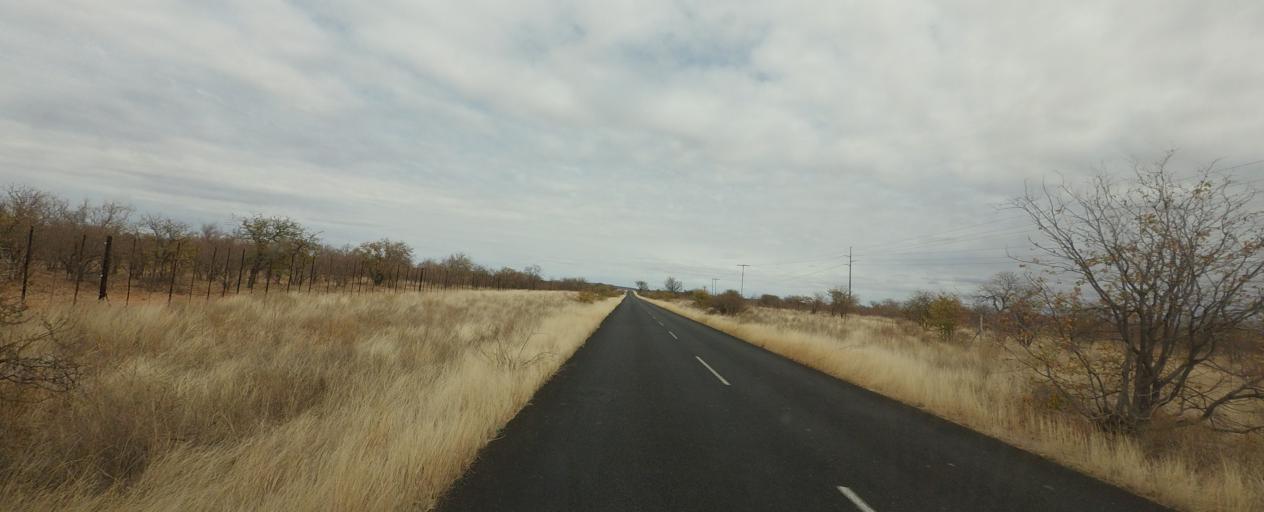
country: ZW
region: Matabeleland South
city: Beitbridge
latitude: -22.4311
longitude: 29.4576
